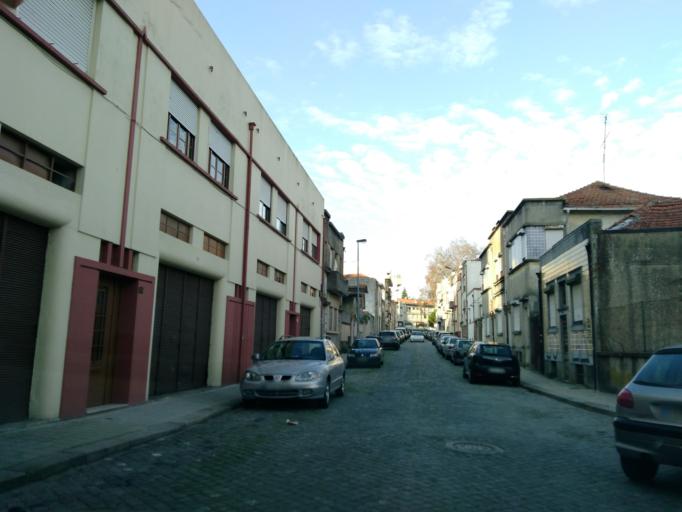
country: PT
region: Porto
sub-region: Porto
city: Porto
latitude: 41.1503
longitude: -8.5904
